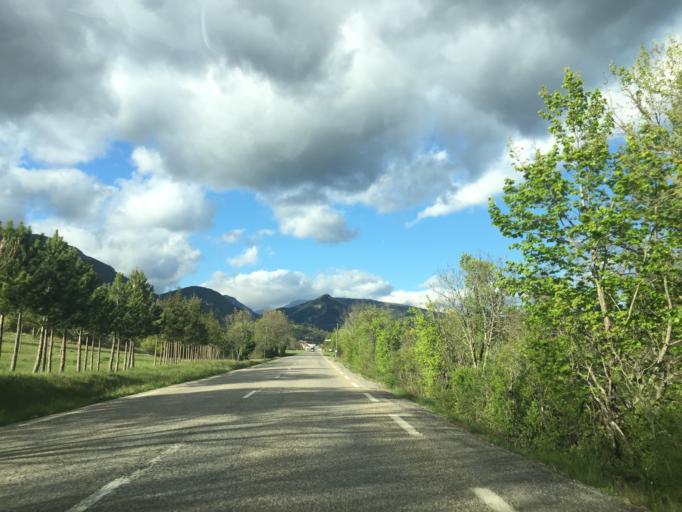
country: FR
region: Provence-Alpes-Cote d'Azur
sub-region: Departement des Hautes-Alpes
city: Veynes
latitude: 44.5131
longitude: 5.7410
